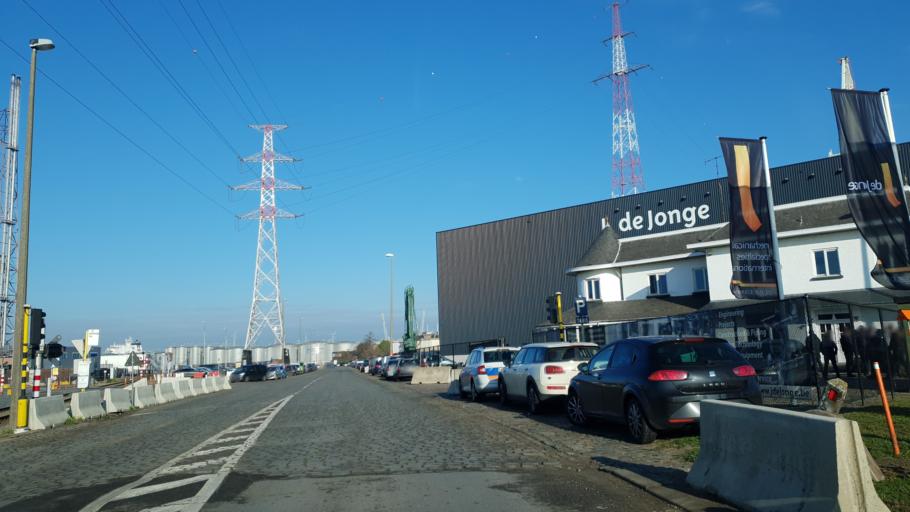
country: BE
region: Flanders
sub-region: Provincie Antwerpen
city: Zwijndrecht
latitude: 51.2564
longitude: 4.3470
